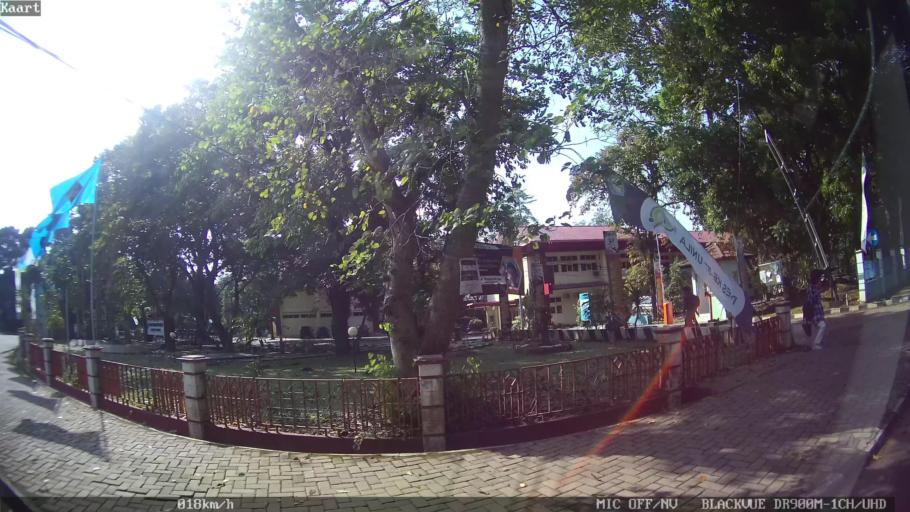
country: ID
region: Lampung
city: Kedaton
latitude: -5.3663
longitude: 105.2436
